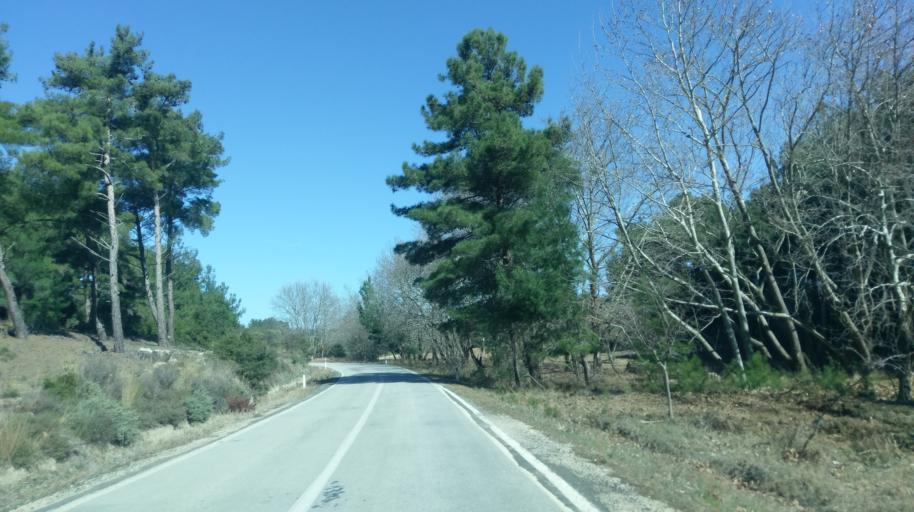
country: TR
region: Canakkale
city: Eceabat
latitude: 40.1204
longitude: 26.2561
